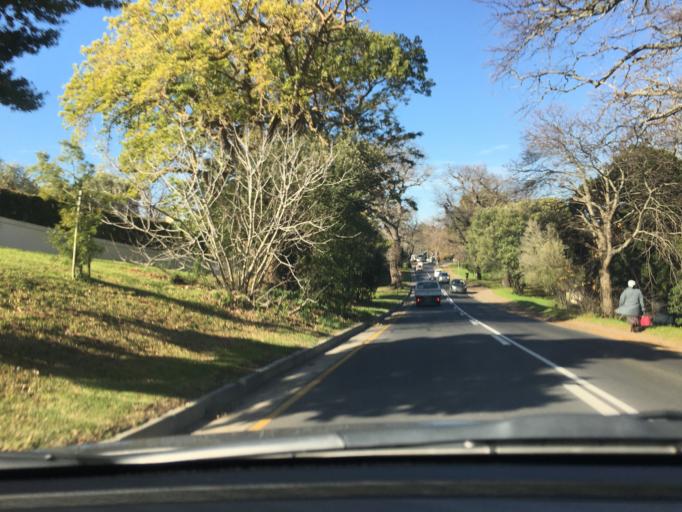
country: ZA
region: Western Cape
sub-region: City of Cape Town
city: Constantia
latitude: -34.0226
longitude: 18.4271
